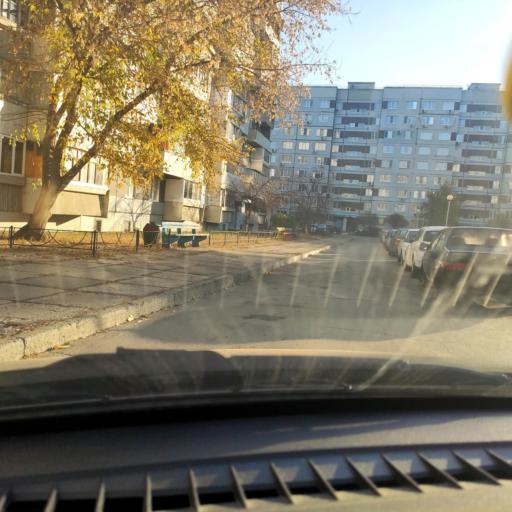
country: RU
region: Samara
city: Tol'yatti
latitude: 53.5346
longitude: 49.3302
